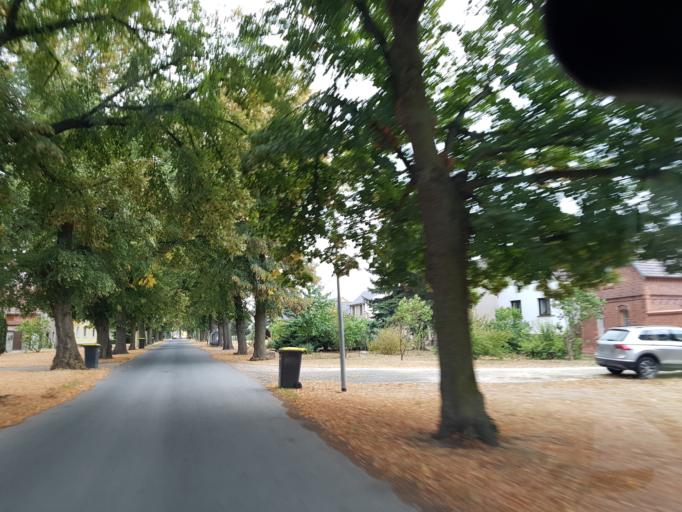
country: DE
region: Brandenburg
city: Herzberg
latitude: 51.6983
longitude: 13.2647
